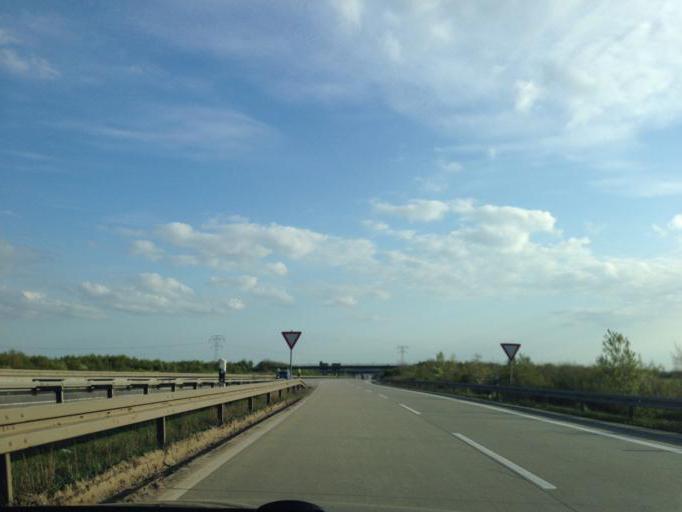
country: DE
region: Saxony-Anhalt
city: Dahlenwarsleben
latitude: 52.1628
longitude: 11.5446
